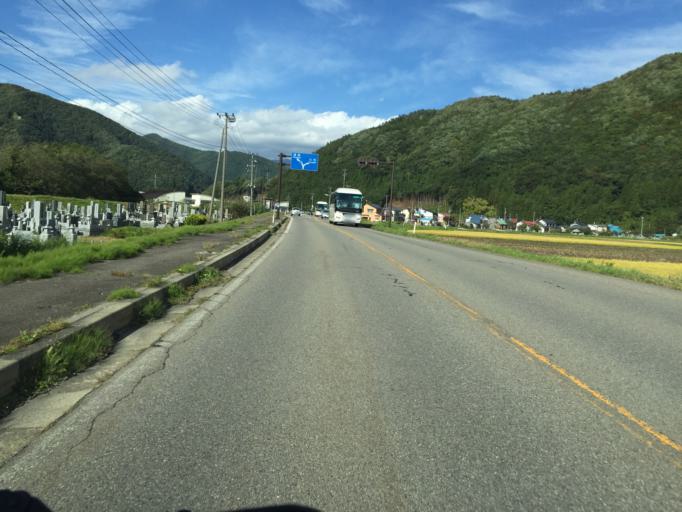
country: JP
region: Fukushima
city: Inawashiro
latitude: 37.5967
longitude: 140.1347
